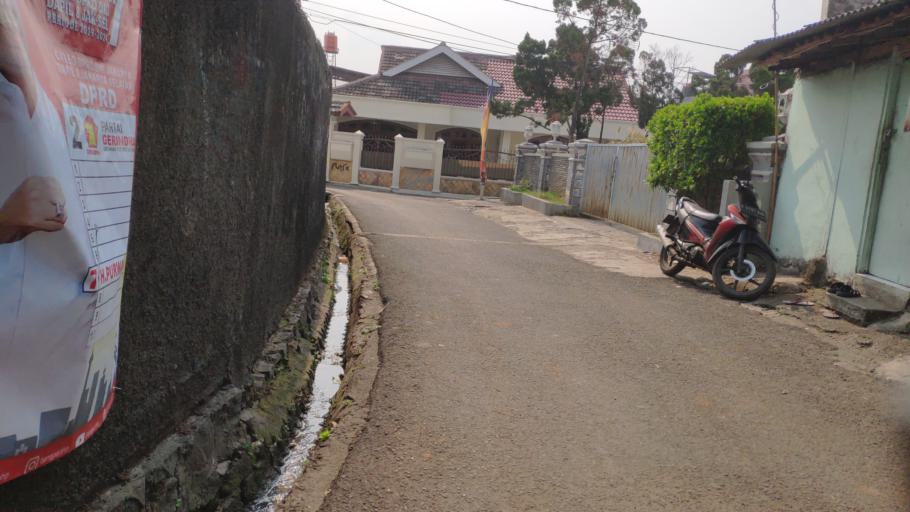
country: ID
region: West Java
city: Depok
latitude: -6.3258
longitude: 106.8140
